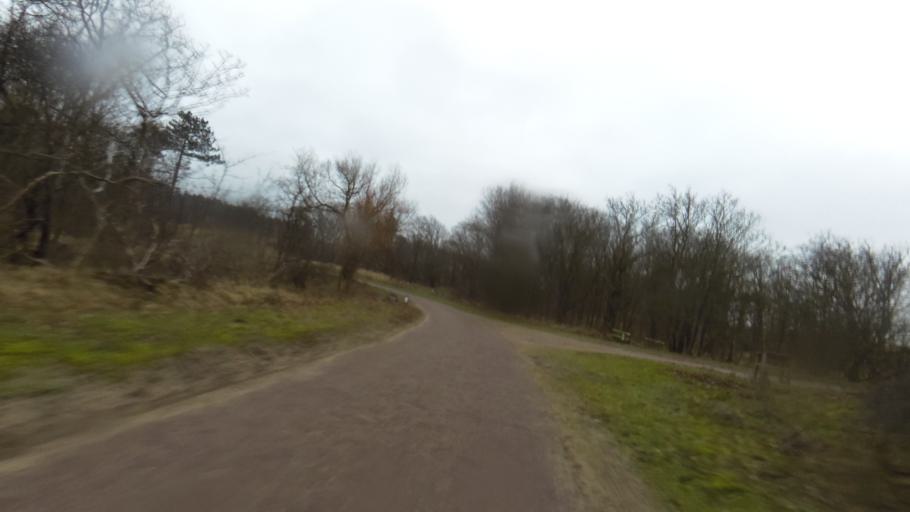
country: NL
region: North Holland
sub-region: Gemeente Bergen
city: Egmond aan Zee
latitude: 52.5763
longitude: 4.6220
